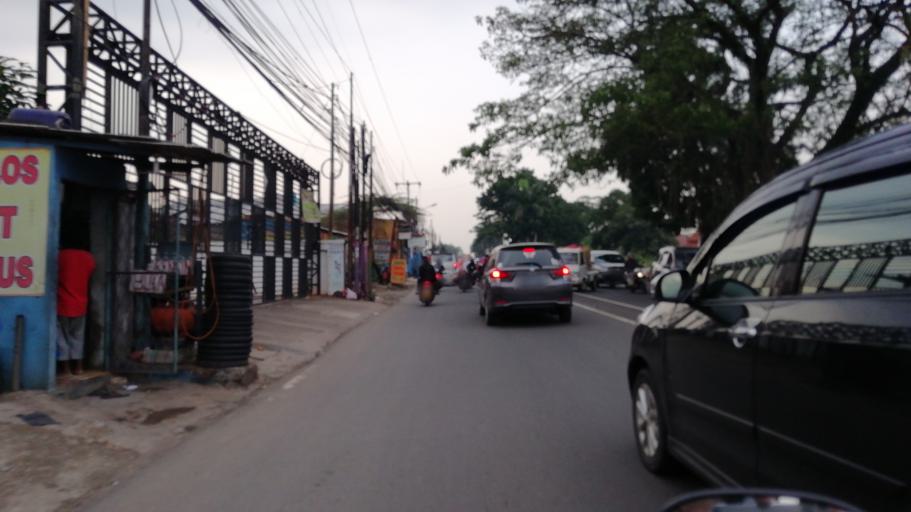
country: ID
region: West Java
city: Cibinong
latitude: -6.4568
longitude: 106.8557
